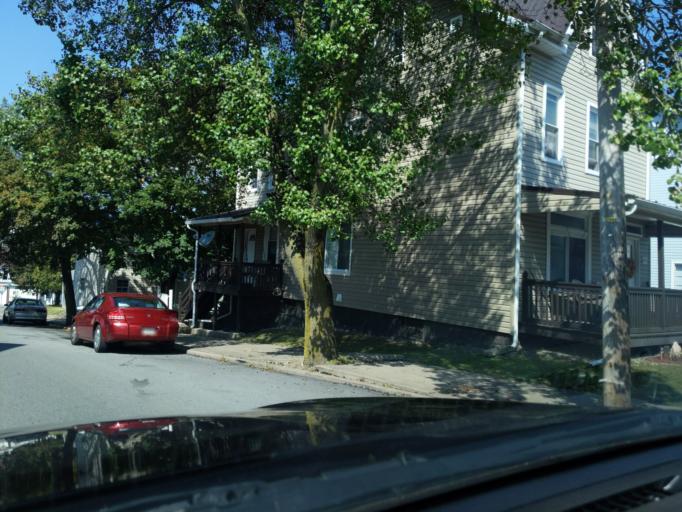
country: US
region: Pennsylvania
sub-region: Blair County
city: Altoona
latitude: 40.5145
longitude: -78.3877
